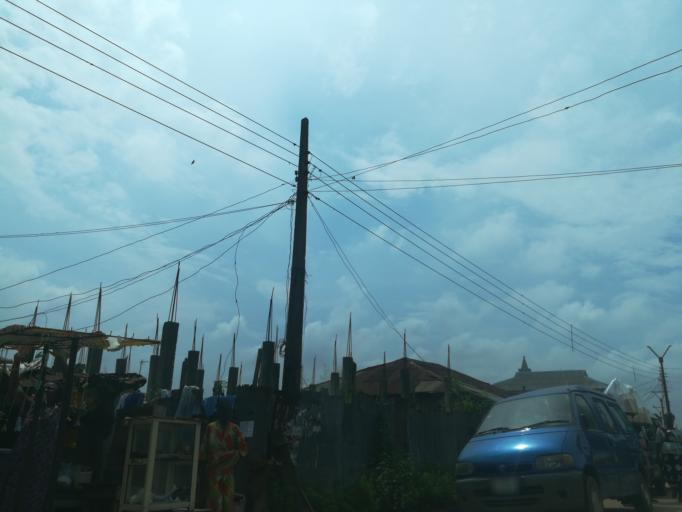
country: NG
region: Lagos
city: Ikorodu
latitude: 6.6152
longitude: 3.5034
